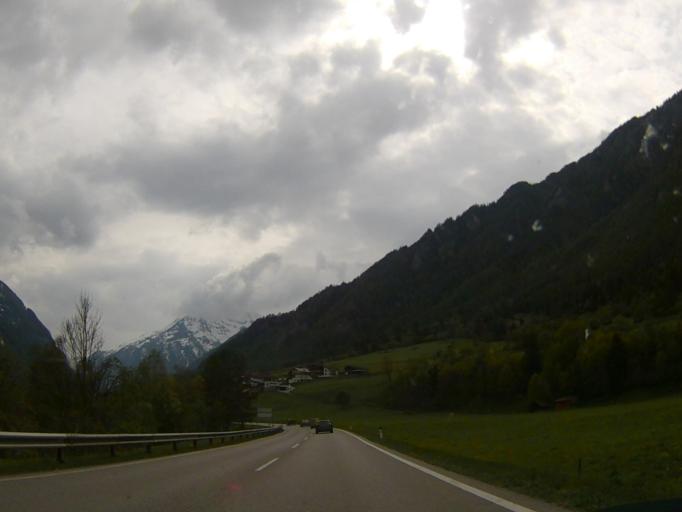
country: AT
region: Tyrol
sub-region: Politischer Bezirk Landeck
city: Pfunds
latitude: 46.9866
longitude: 10.5674
